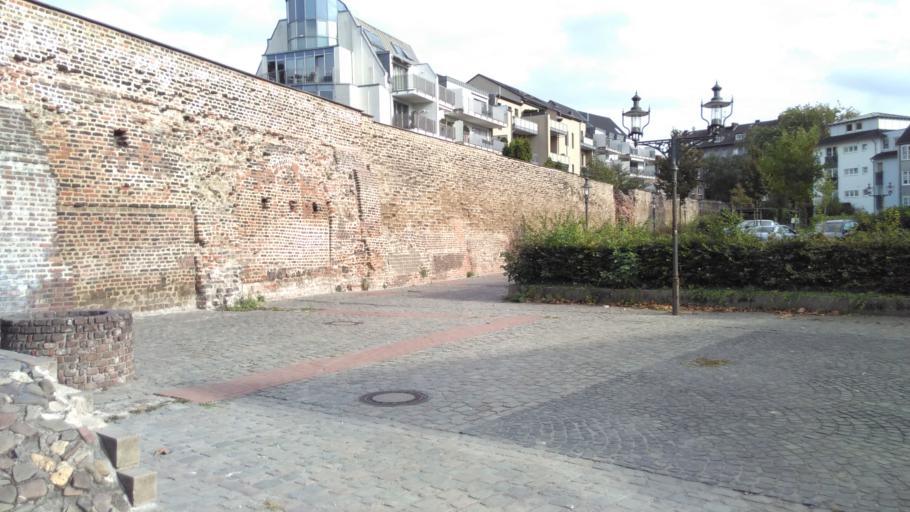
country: DE
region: North Rhine-Westphalia
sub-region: Regierungsbezirk Dusseldorf
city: Duisburg
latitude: 51.4382
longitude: 6.7644
